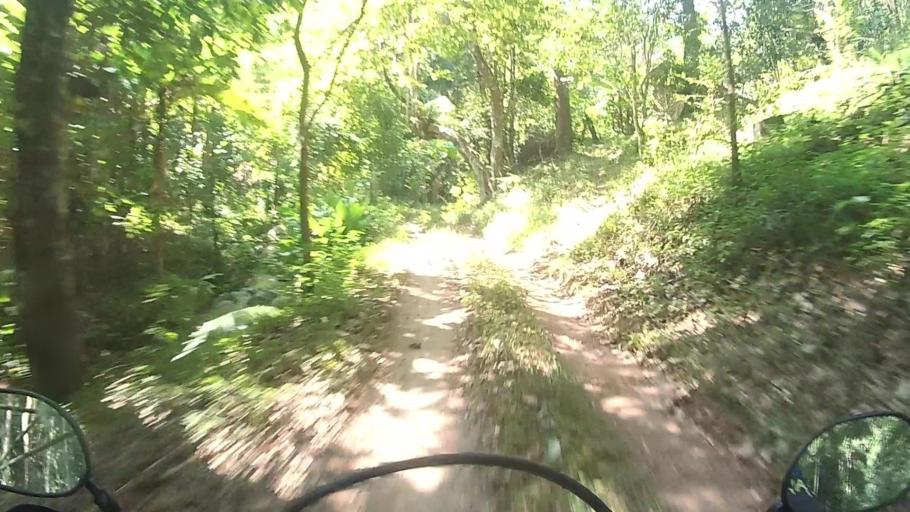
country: TH
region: Chiang Mai
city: Mae On
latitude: 19.0583
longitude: 99.3328
